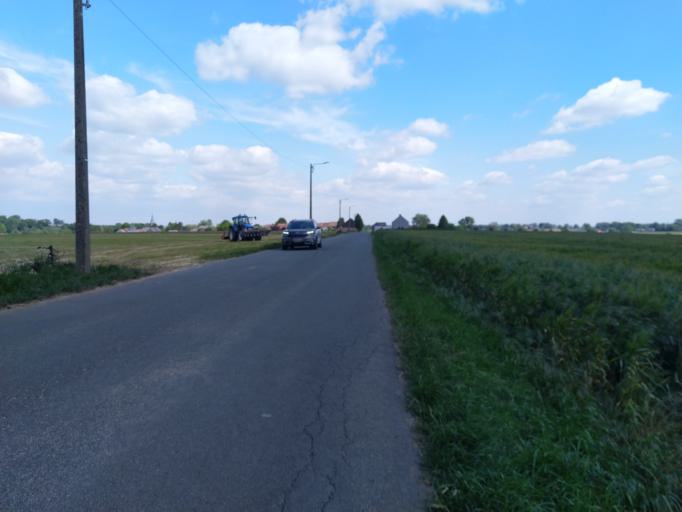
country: BE
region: Wallonia
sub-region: Province du Hainaut
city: Soignies
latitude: 50.5991
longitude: 4.0390
